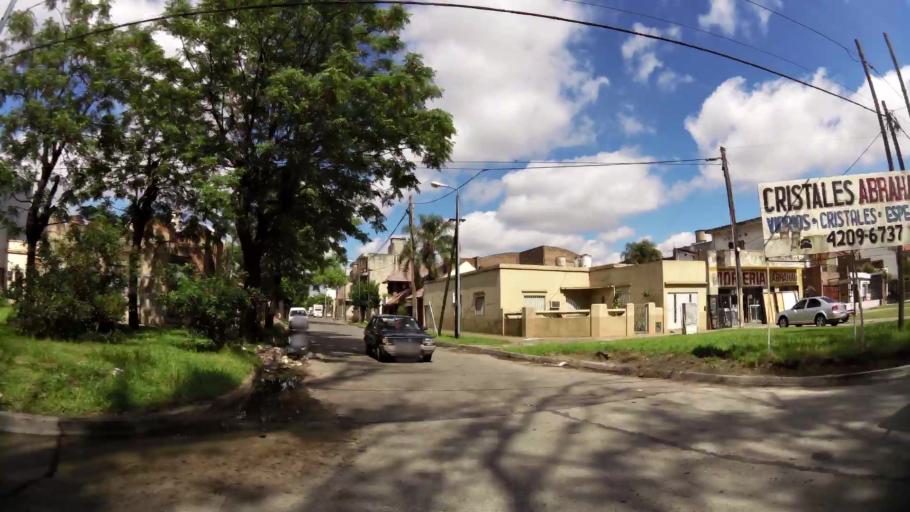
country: AR
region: Buenos Aires
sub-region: Partido de Lanus
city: Lanus
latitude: -34.6865
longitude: -58.4175
